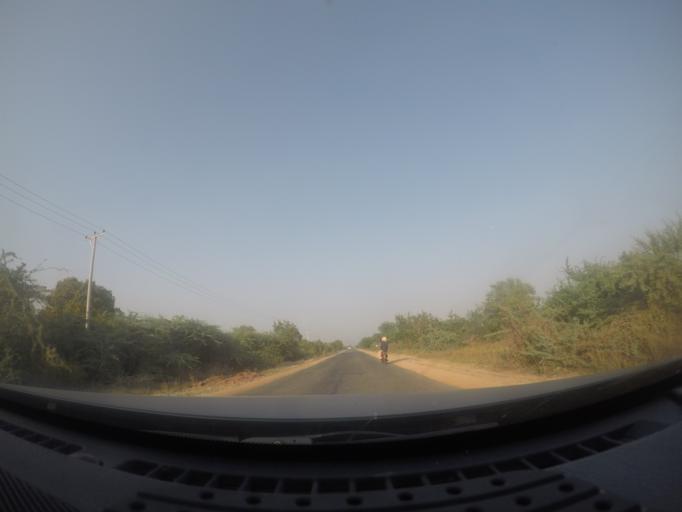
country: MM
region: Mandalay
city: Yamethin
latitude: 20.6544
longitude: 96.1109
